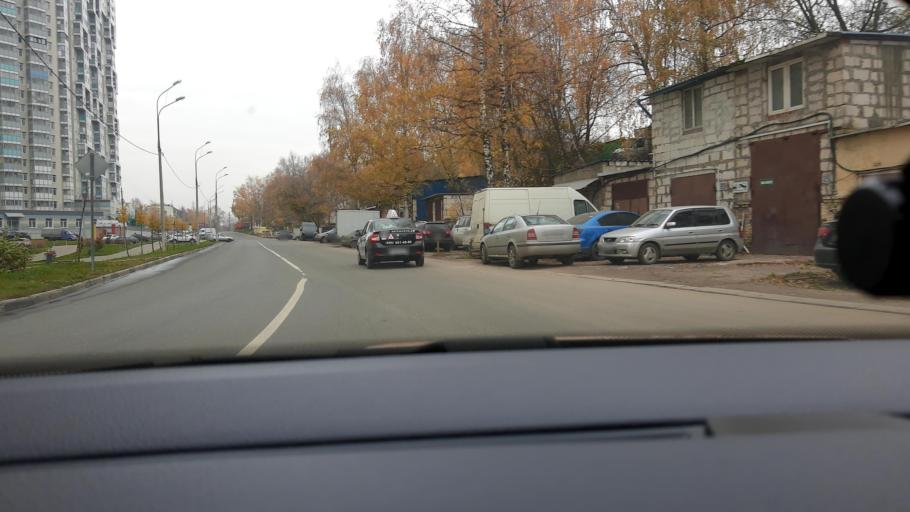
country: RU
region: Moskovskaya
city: Cherkizovo
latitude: 55.9435
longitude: 37.7732
